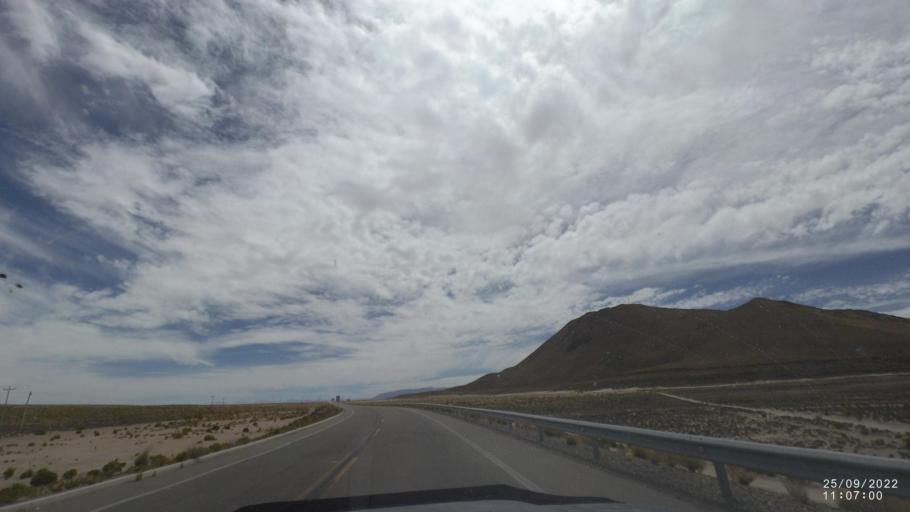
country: BO
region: Oruro
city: Challapata
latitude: -19.3516
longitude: -66.8554
